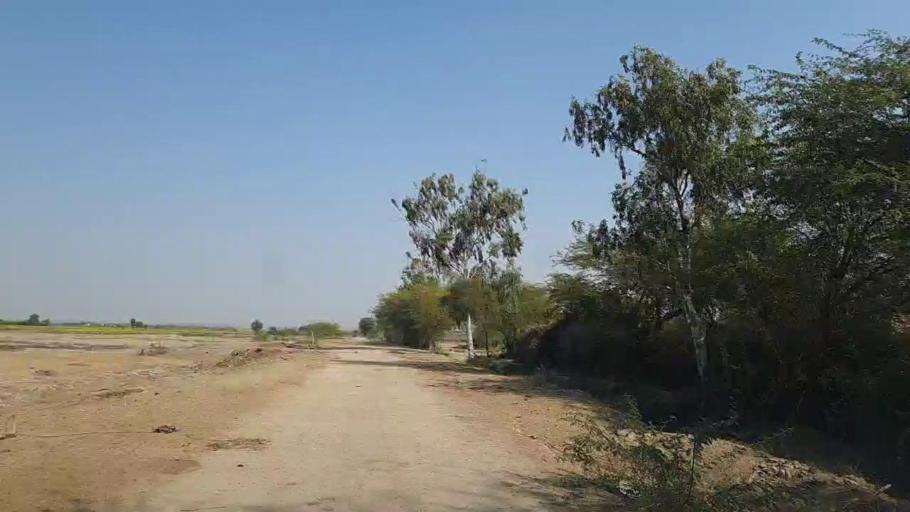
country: PK
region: Sindh
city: Naukot
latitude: 24.8934
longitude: 69.4706
